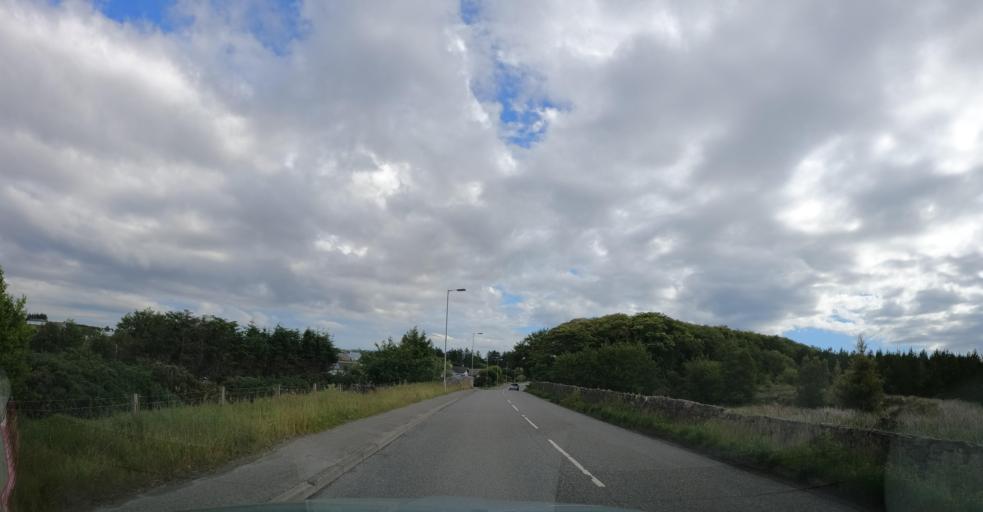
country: GB
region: Scotland
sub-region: Eilean Siar
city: Isle of Lewis
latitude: 58.2147
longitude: -6.4134
